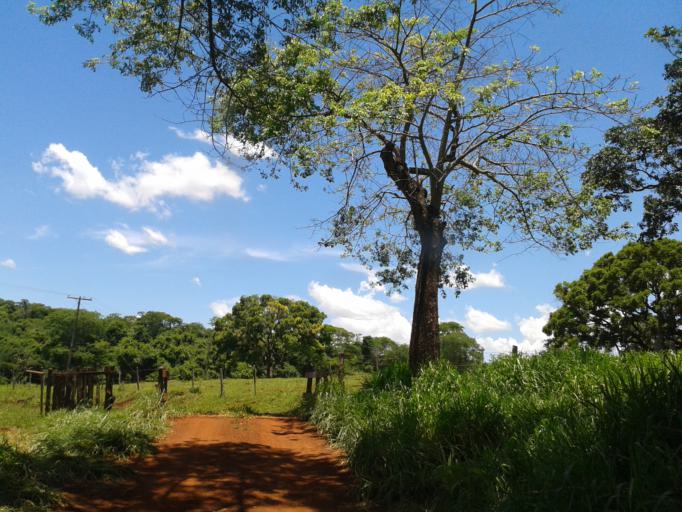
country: BR
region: Minas Gerais
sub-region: Centralina
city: Centralina
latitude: -18.7018
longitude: -49.1815
